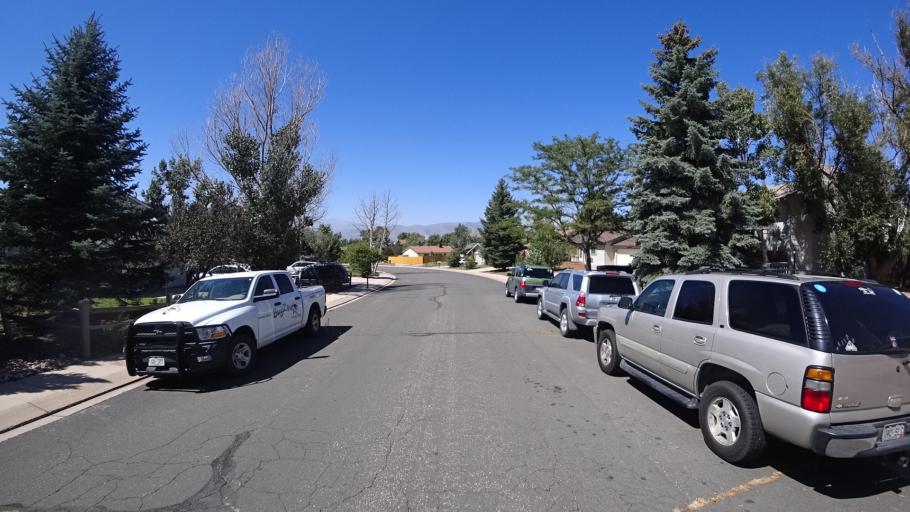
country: US
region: Colorado
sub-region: El Paso County
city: Black Forest
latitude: 38.9471
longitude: -104.7595
